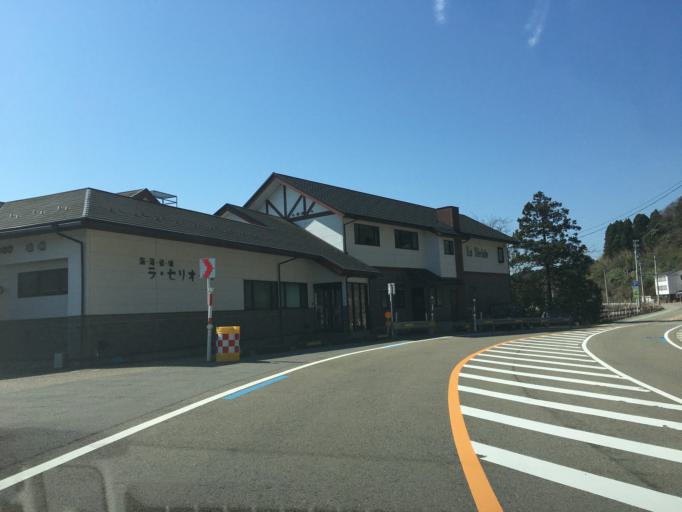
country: JP
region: Toyama
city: Himi
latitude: 36.8999
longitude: 137.0113
